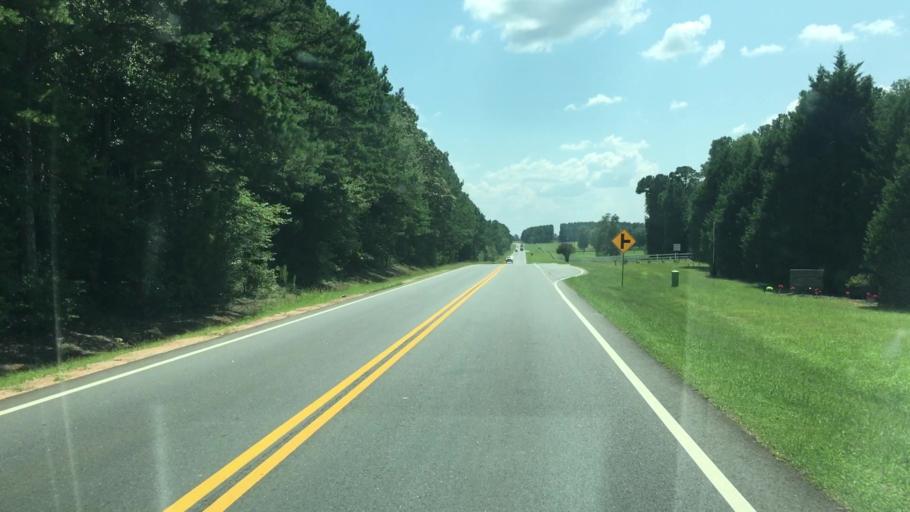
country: US
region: Georgia
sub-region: Oconee County
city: Watkinsville
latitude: 33.7648
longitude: -83.4336
